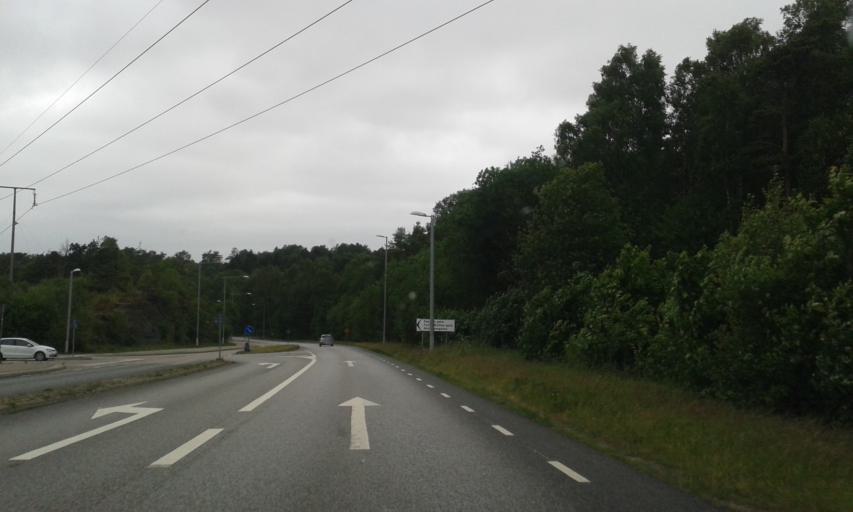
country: SE
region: Vaestra Goetaland
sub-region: Goteborg
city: Eriksbo
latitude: 57.7644
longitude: 12.0558
